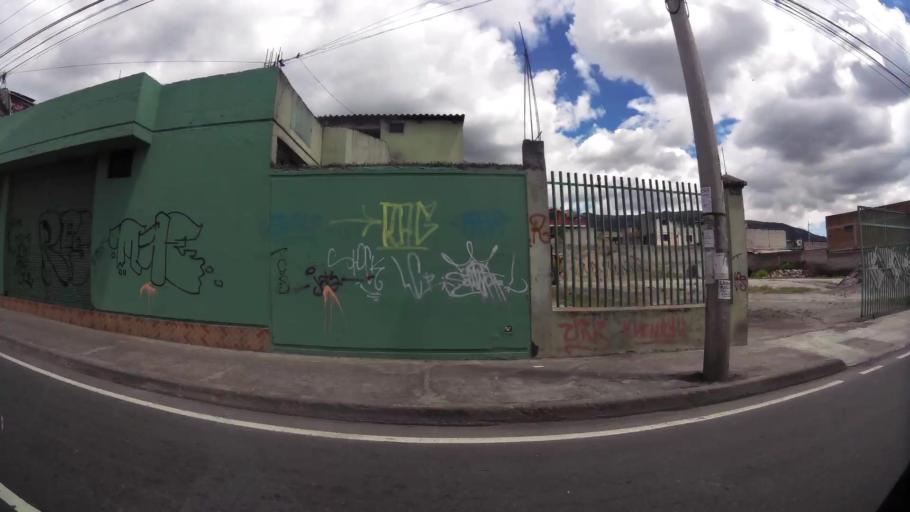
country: EC
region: Pichincha
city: Sangolqui
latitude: -0.3355
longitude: -78.5502
